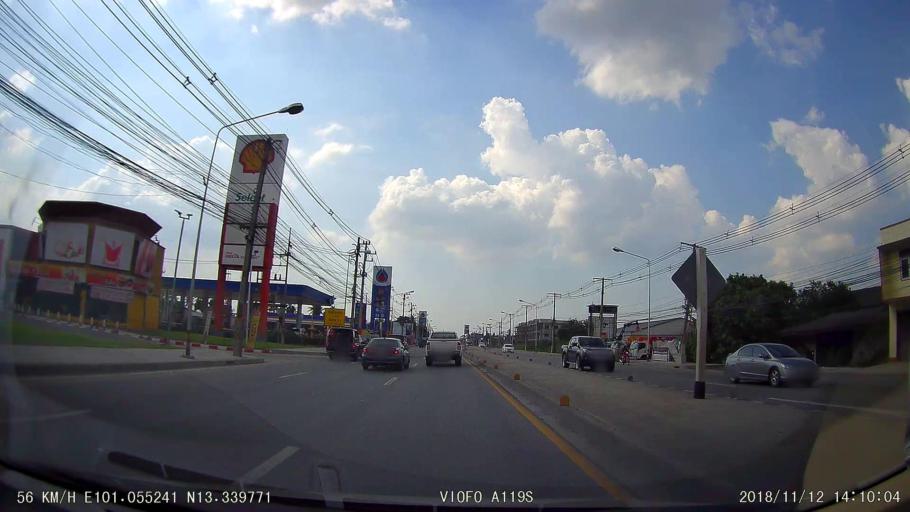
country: TH
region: Chon Buri
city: Ban Bueng
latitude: 13.3398
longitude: 101.0551
